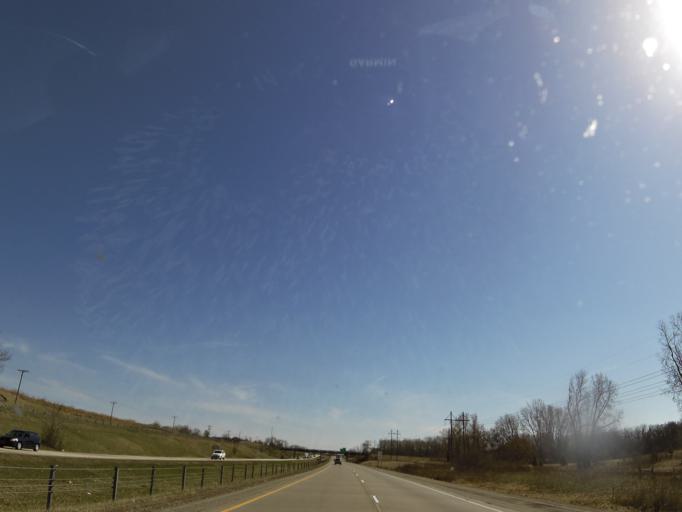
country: US
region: Minnesota
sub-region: Dakota County
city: Lakeville
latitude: 44.6706
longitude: -93.2944
